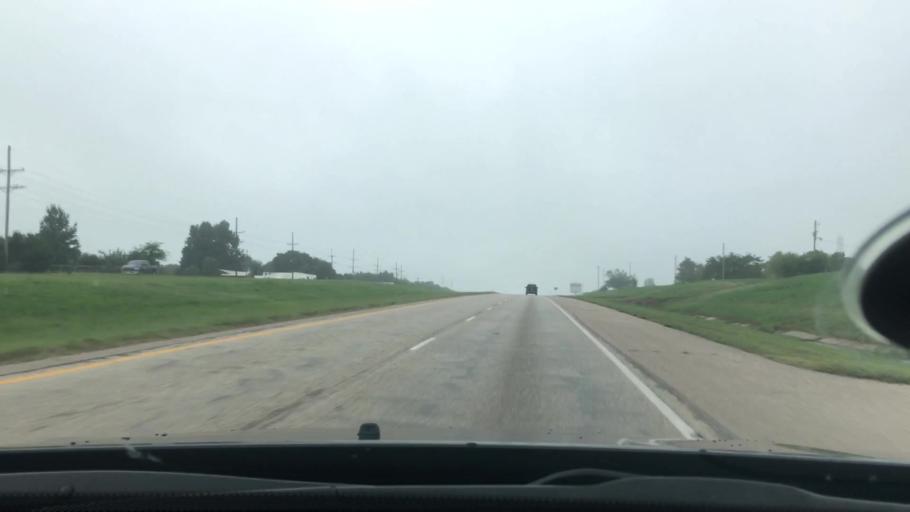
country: US
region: Oklahoma
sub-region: Seminole County
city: Seminole
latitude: 35.2863
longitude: -96.6707
